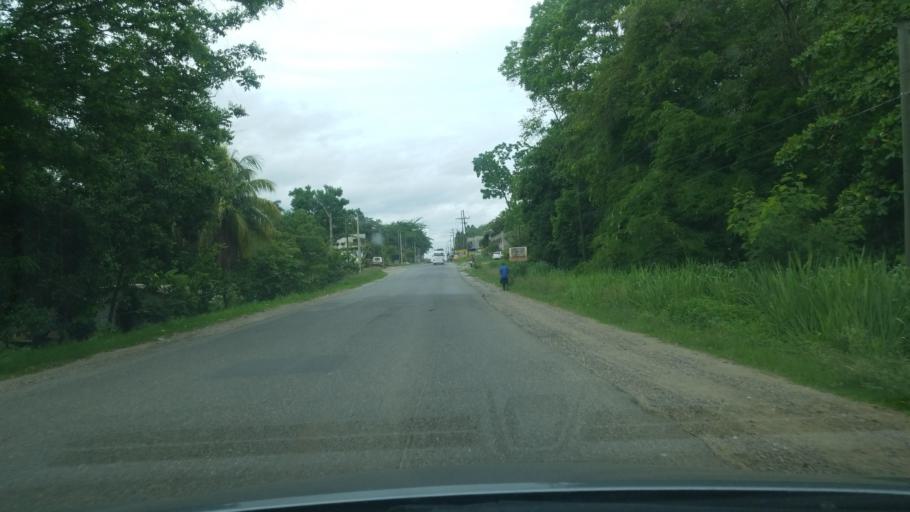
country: HN
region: Santa Barbara
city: La Flecha
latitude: 15.2972
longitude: -88.4848
